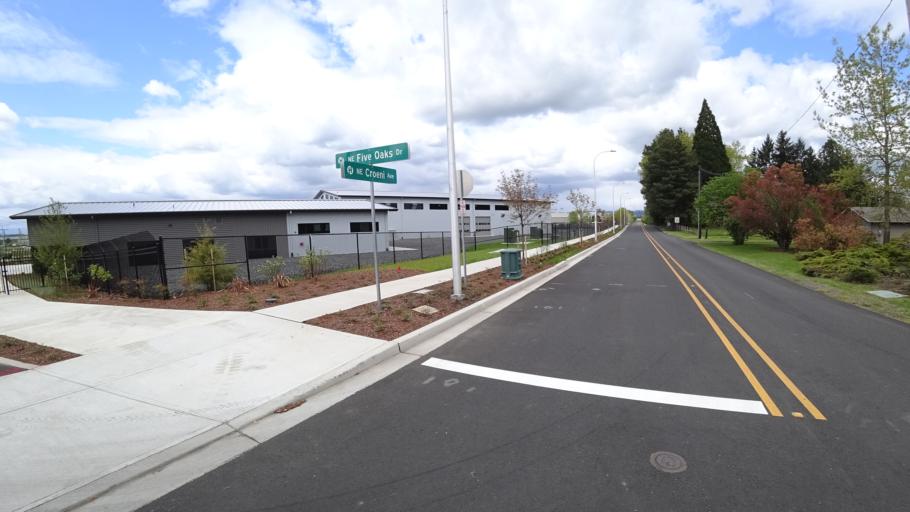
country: US
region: Oregon
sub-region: Washington County
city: Rockcreek
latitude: 45.5575
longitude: -122.9056
